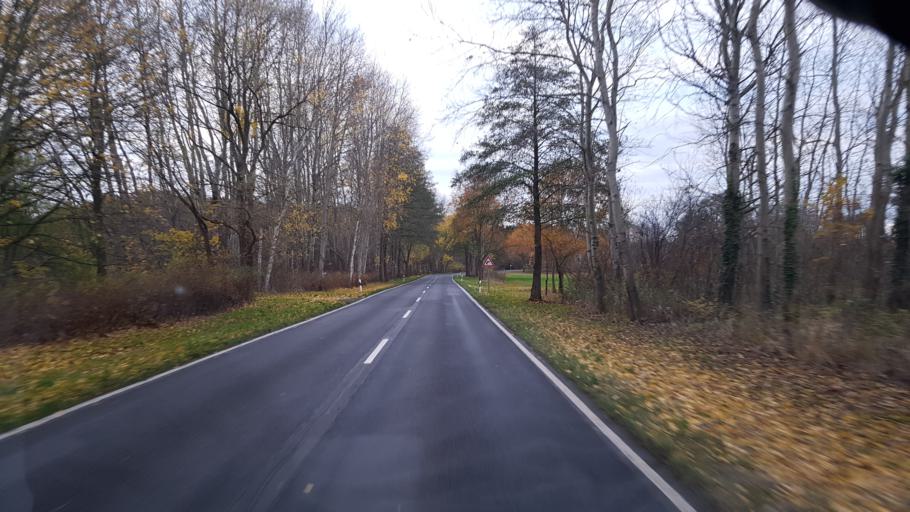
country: DE
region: Brandenburg
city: Kroppen
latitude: 51.3836
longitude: 13.7847
